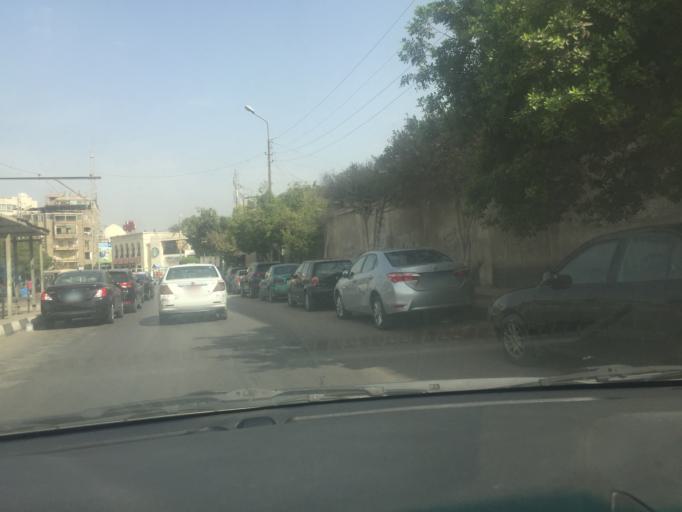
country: EG
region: Muhafazat al Qahirah
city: Cairo
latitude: 30.0849
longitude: 31.3478
